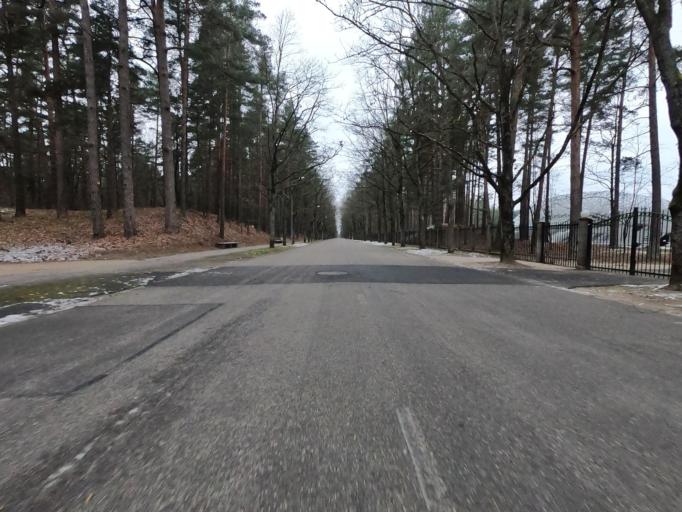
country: LV
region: Riga
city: Jaunciems
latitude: 57.0132
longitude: 24.1522
